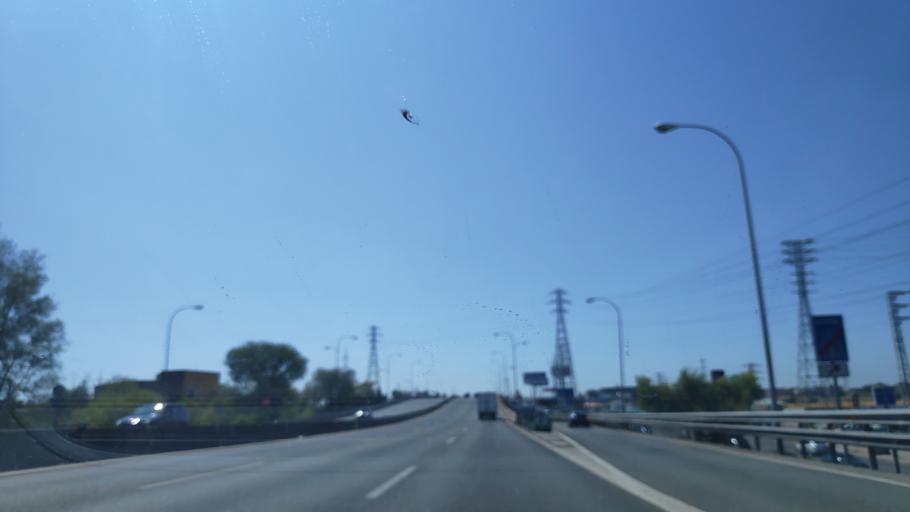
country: ES
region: Madrid
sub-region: Provincia de Madrid
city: Villaverde
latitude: 40.3400
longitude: -3.7243
